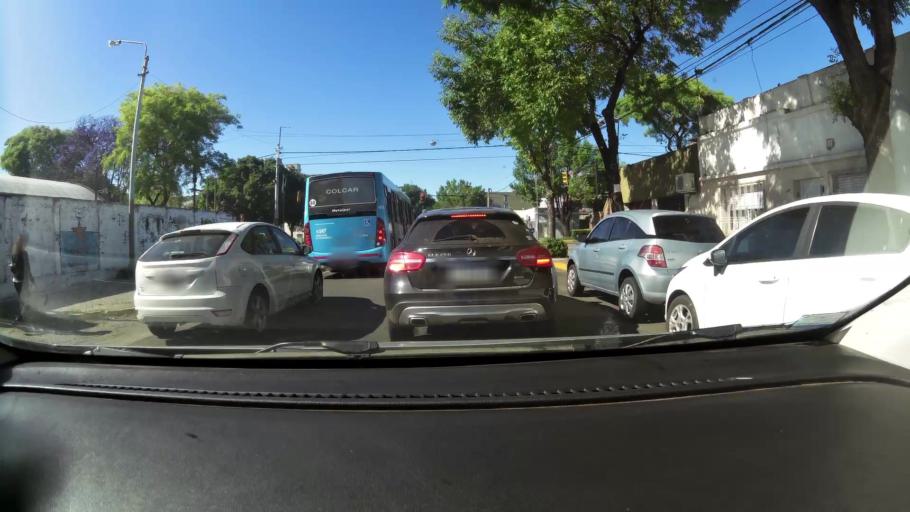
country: AR
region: Santa Fe
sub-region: Departamento de Rosario
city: Rosario
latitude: -32.9523
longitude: -60.6668
